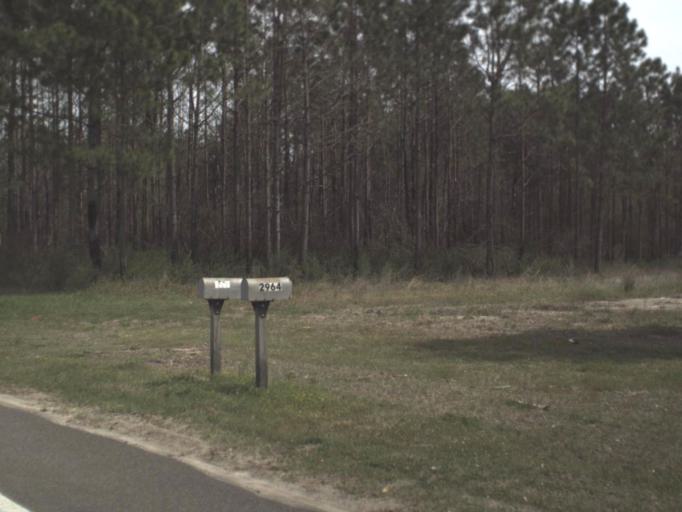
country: US
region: Alabama
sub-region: Geneva County
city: Hartford
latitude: 30.9594
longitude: -85.7059
